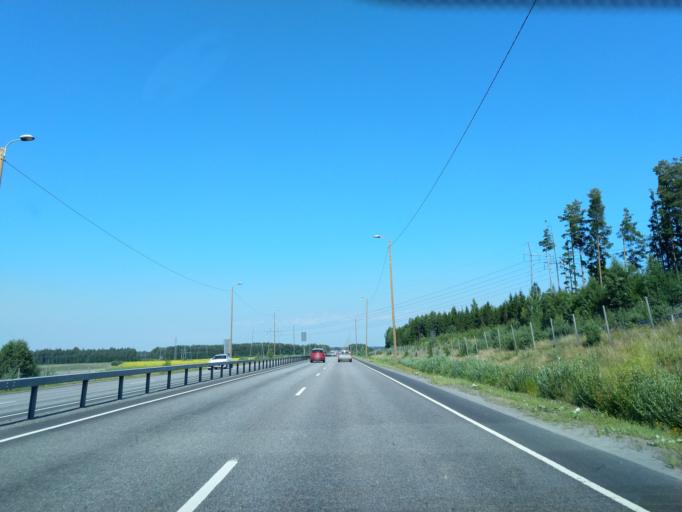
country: FI
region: Satakunta
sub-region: Pori
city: Nakkila
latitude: 61.3369
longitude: 22.0464
